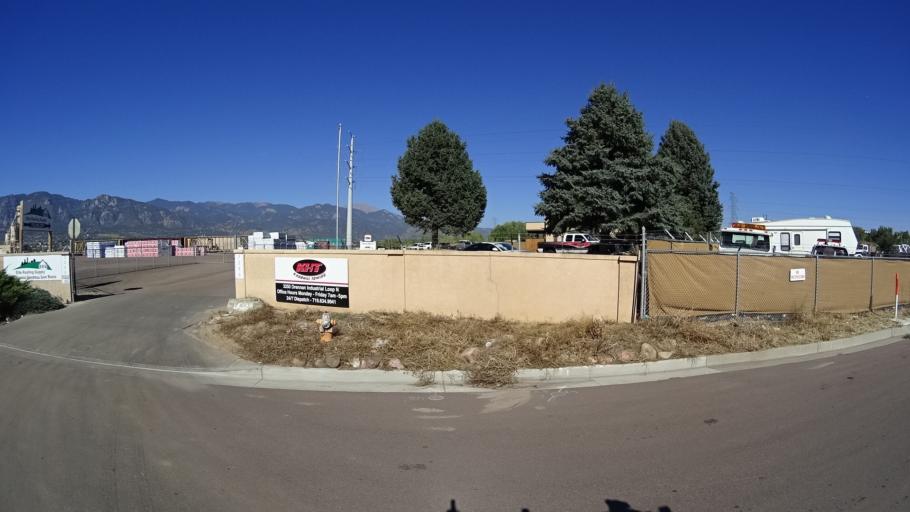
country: US
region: Colorado
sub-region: El Paso County
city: Stratmoor
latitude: 38.7869
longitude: -104.7699
